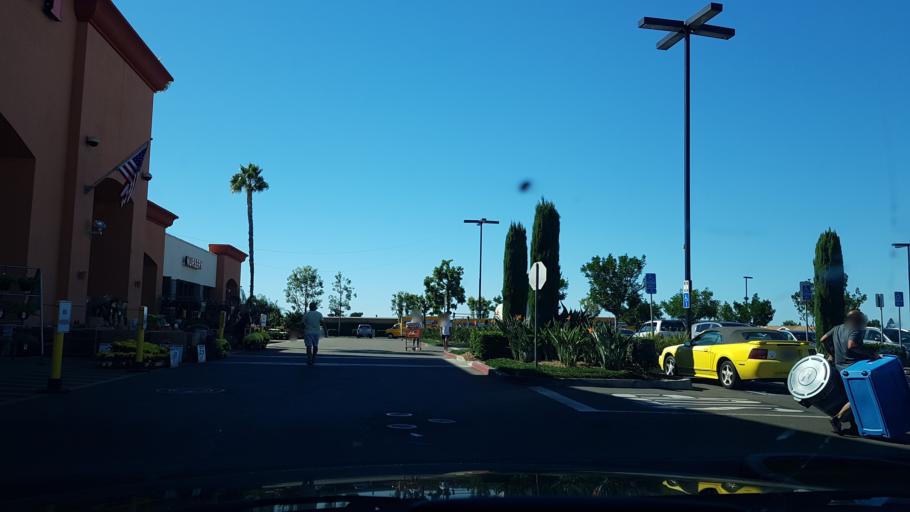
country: US
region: California
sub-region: San Diego County
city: Poway
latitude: 32.9141
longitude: -117.1215
